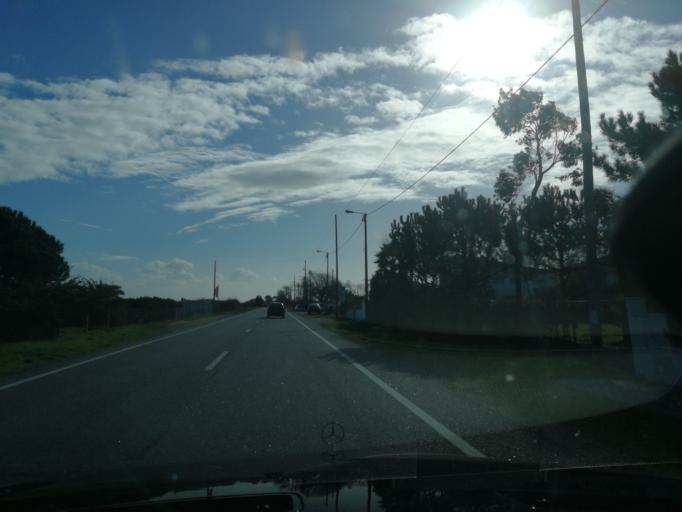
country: PT
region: Aveiro
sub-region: Estarreja
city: Pardilho
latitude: 40.8155
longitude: -8.6704
